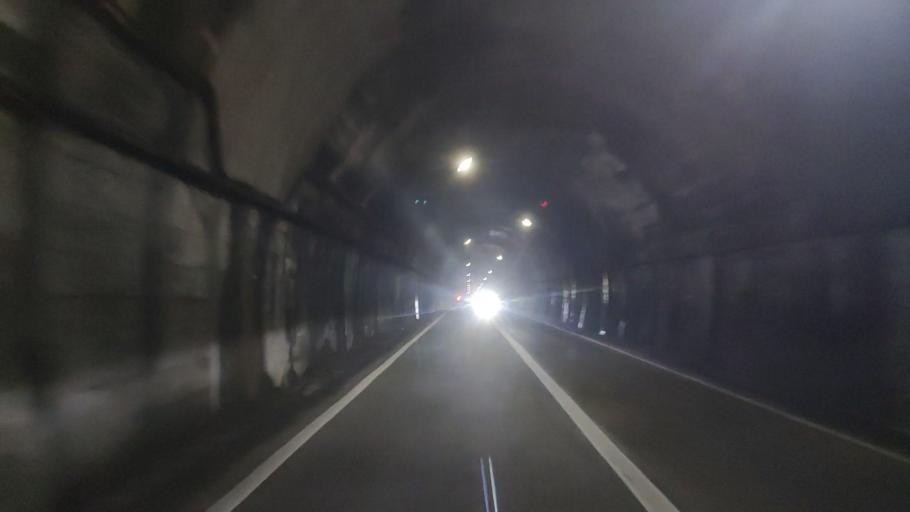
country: JP
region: Mie
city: Ise
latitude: 34.4583
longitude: 136.7356
